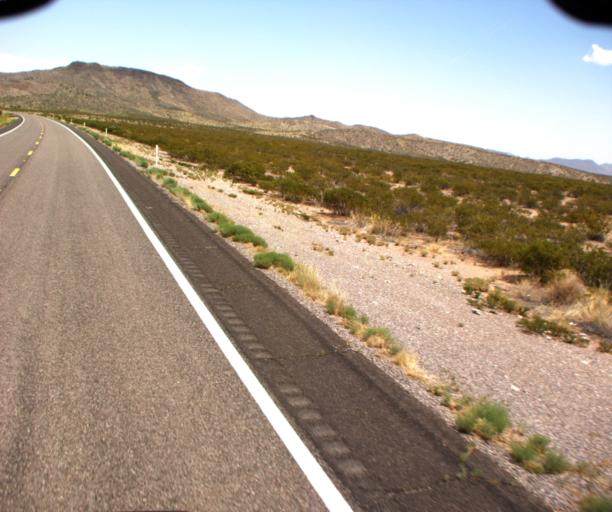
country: US
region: Arizona
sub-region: Greenlee County
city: Clifton
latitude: 32.7516
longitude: -109.3415
